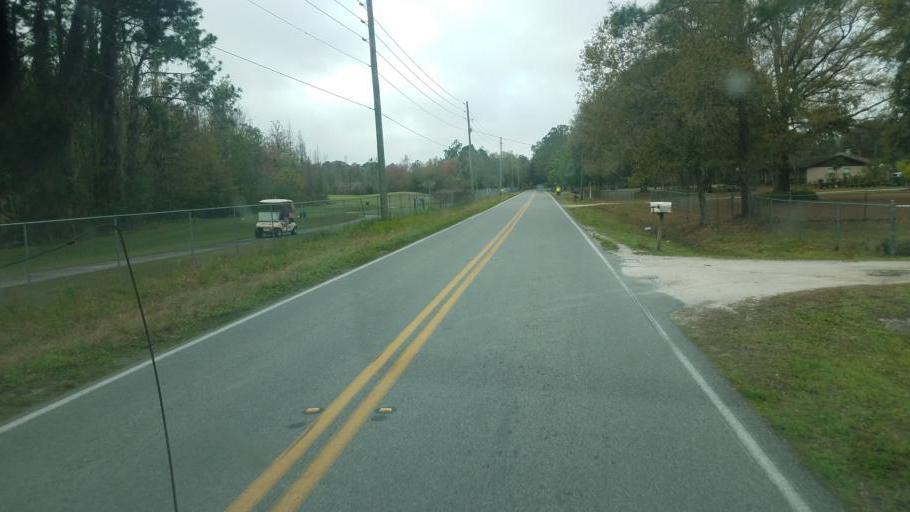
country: US
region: Florida
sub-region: Polk County
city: Kathleen
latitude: 28.1904
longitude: -82.0052
